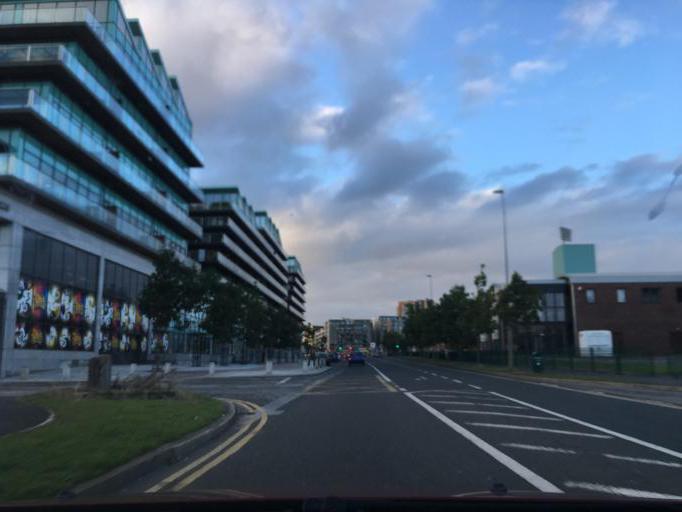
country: IE
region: Leinster
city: Tallaght
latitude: 53.2826
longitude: -6.3751
